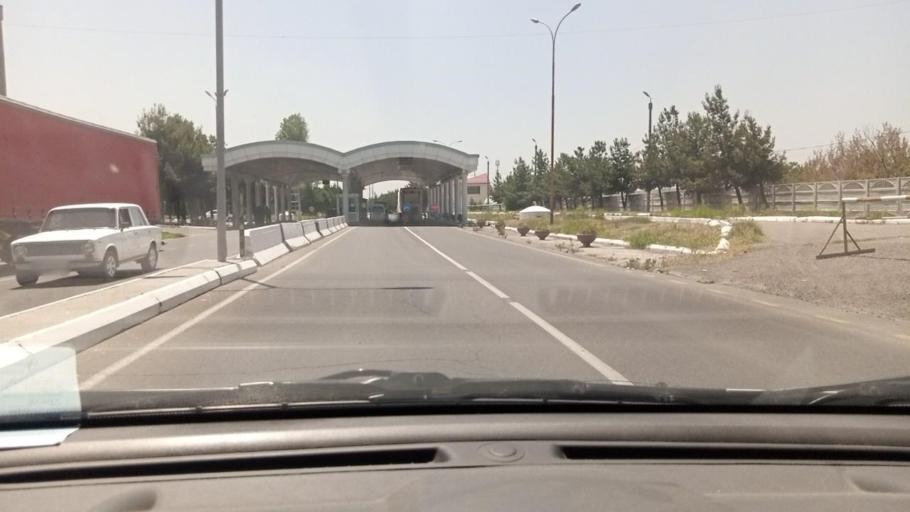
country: UZ
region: Toshkent
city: Urtaowul
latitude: 41.2157
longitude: 69.1732
